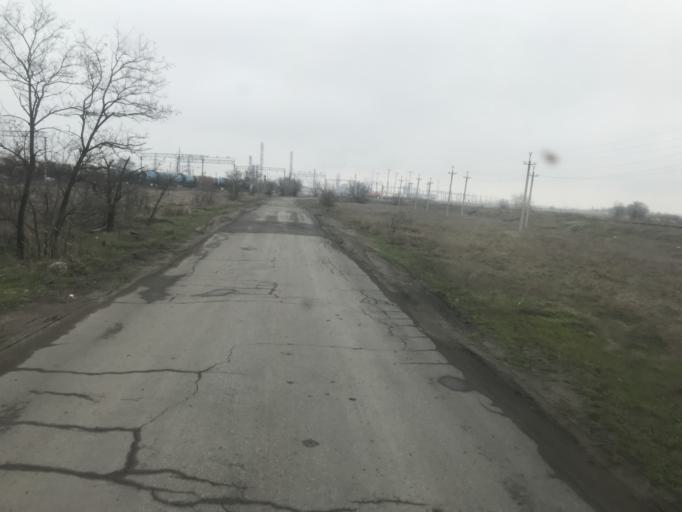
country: RU
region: Volgograd
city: Svetlyy Yar
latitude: 48.4934
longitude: 44.6550
